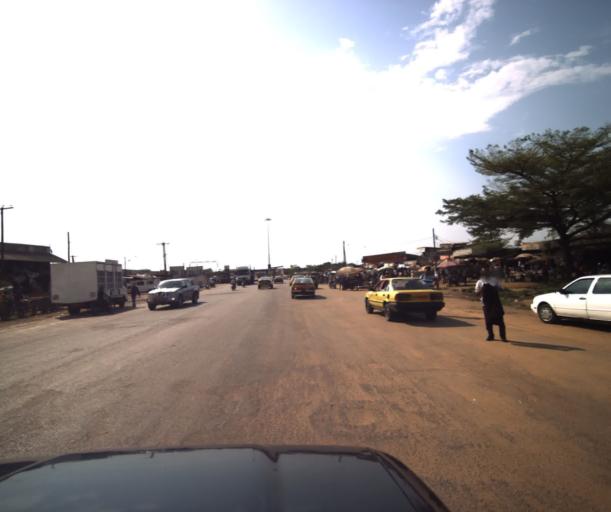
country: CM
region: Littoral
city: Douala
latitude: 4.0190
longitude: 9.7235
